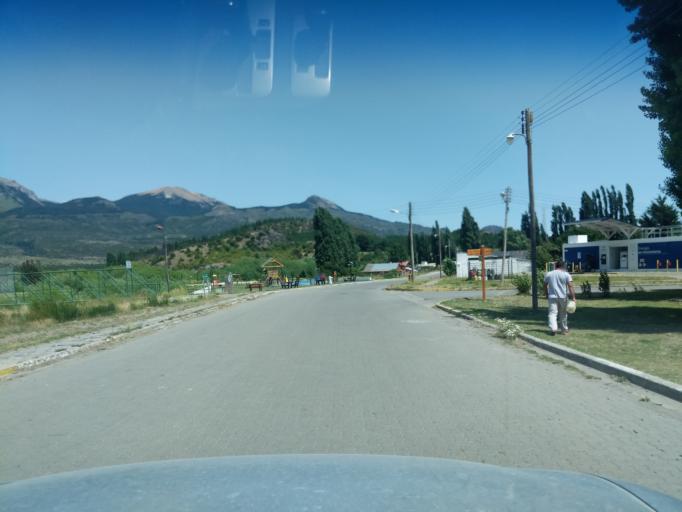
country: CL
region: Los Lagos
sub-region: Provincia de Palena
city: Palena
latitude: -43.5361
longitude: -71.4729
